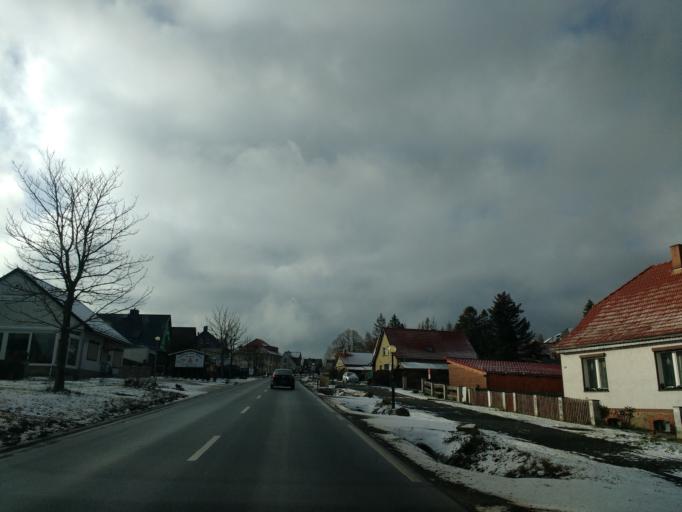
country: DE
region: Saxony-Anhalt
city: Friedrichsbrunn
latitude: 51.6867
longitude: 11.0329
